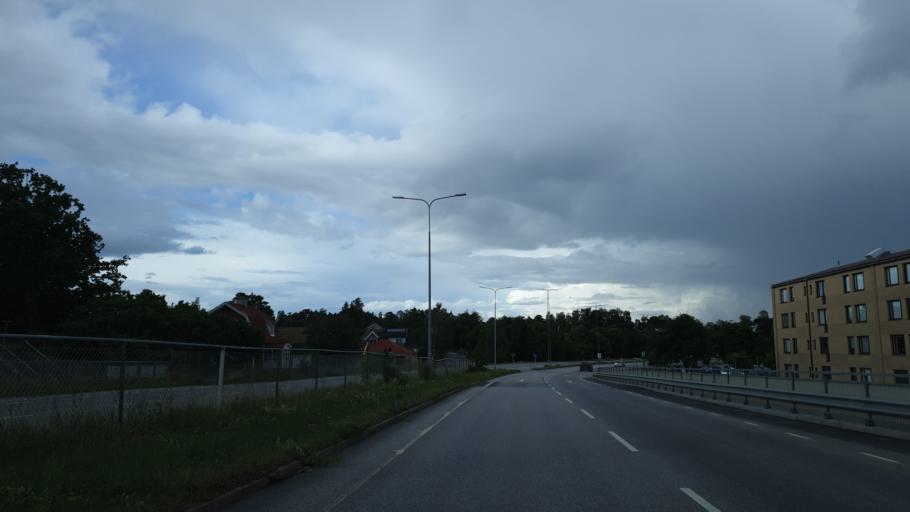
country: SE
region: Stockholm
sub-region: Jarfalla Kommun
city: Jakobsberg
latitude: 59.4234
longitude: 17.8202
